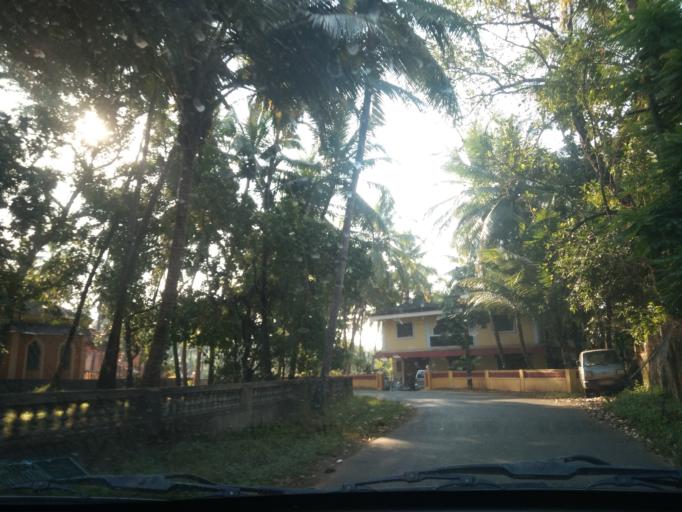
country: IN
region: Goa
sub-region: South Goa
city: Chinchinim
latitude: 15.2081
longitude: 73.9802
